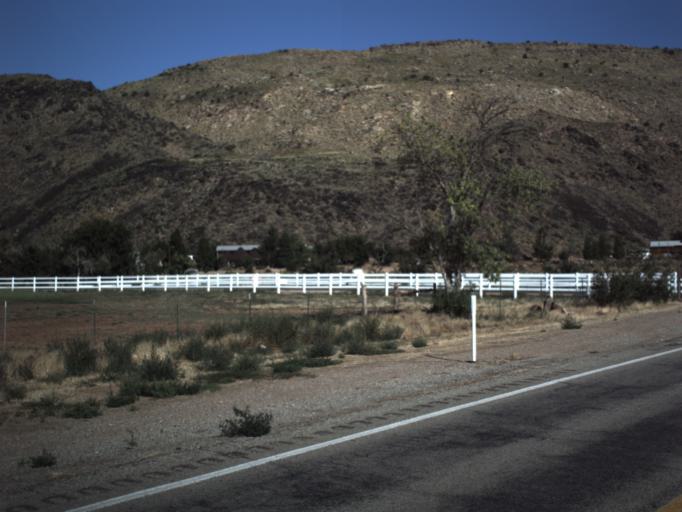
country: US
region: Utah
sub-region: Washington County
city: Toquerville
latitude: 37.2600
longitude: -113.2872
